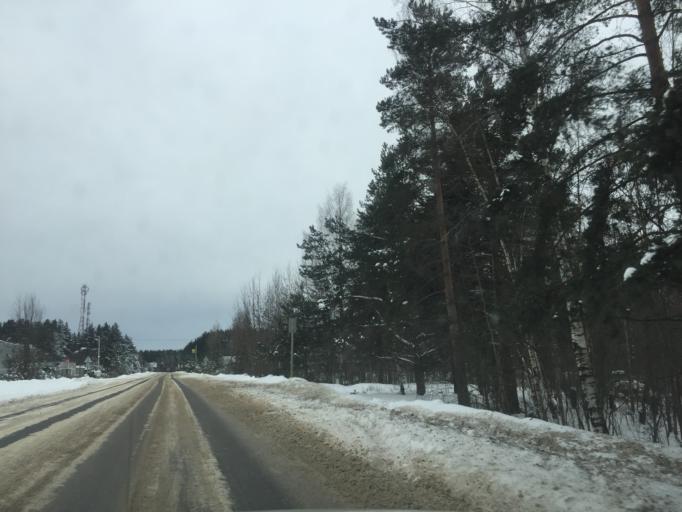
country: RU
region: Leningrad
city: Imeni Sverdlova
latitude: 59.8634
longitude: 30.6712
